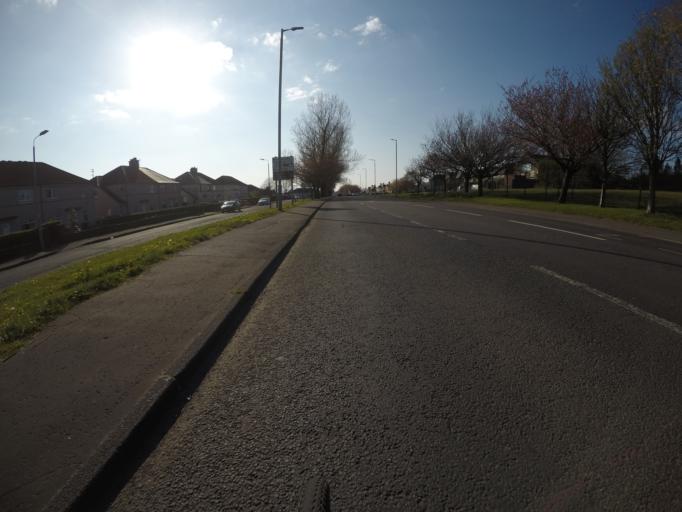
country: GB
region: Scotland
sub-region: North Ayrshire
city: Saltcoats
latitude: 55.6416
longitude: -4.7782
